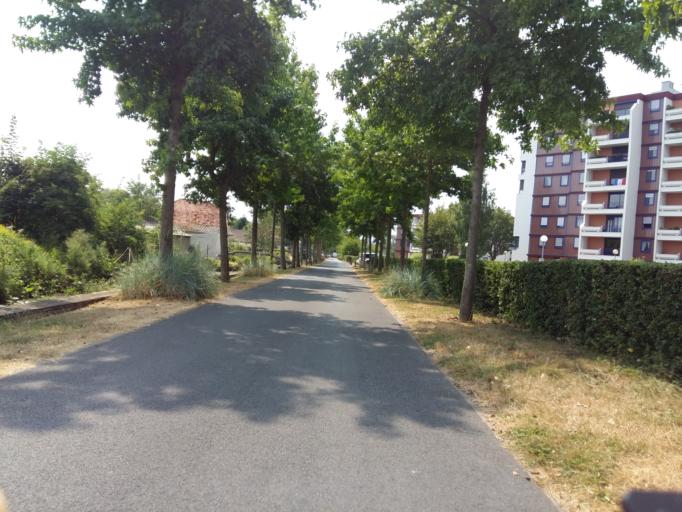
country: FR
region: Picardie
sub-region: Departement de la Somme
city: Rivery
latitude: 49.8985
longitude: 2.3170
